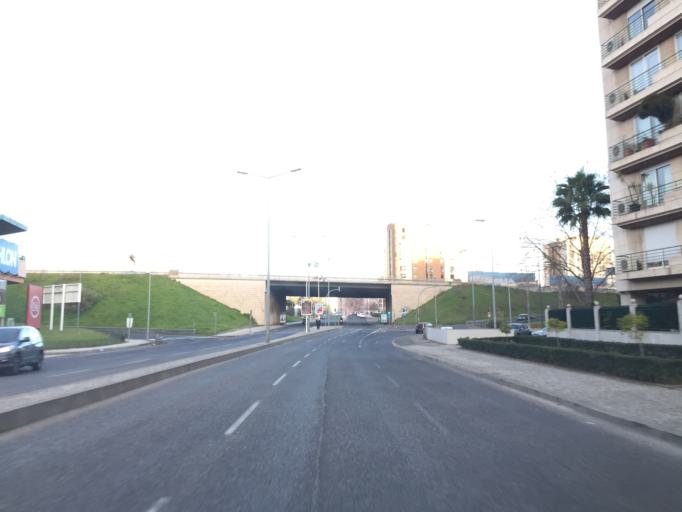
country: PT
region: Lisbon
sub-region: Odivelas
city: Pontinha
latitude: 38.7639
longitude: -9.1746
